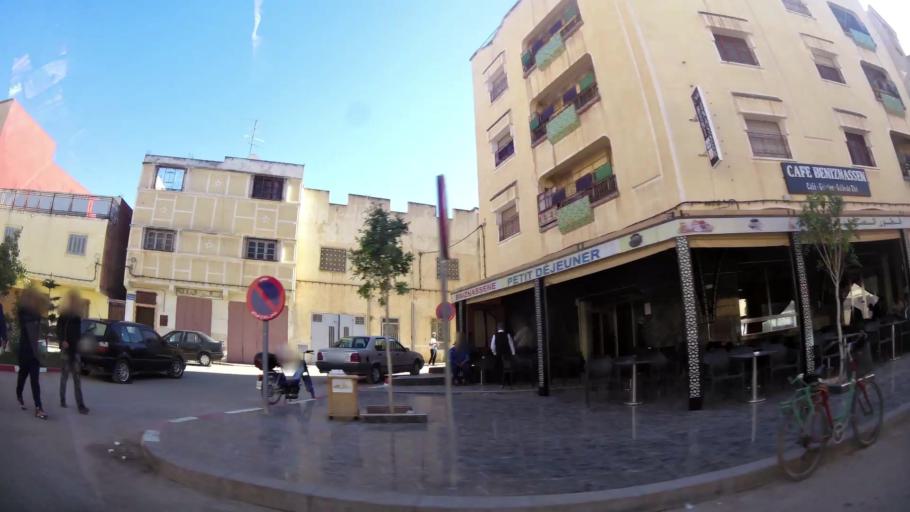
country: MA
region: Oriental
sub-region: Berkane-Taourirt
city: Ahfir
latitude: 34.9557
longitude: -2.1031
